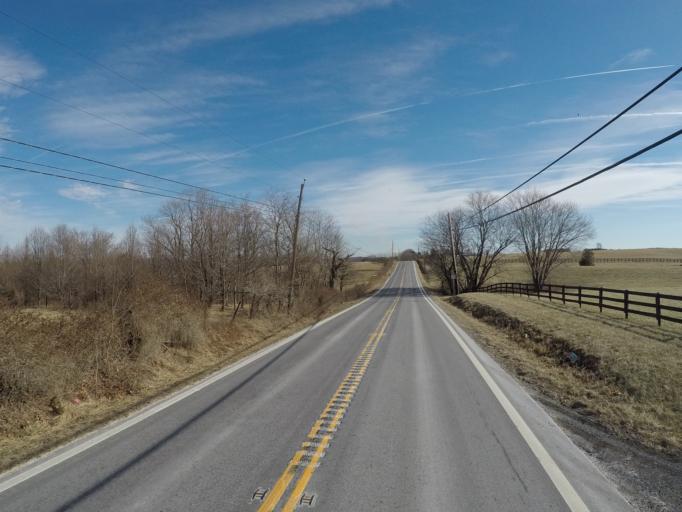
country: US
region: Maryland
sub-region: Frederick County
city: Point of Rocks
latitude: 39.2524
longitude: -77.5347
